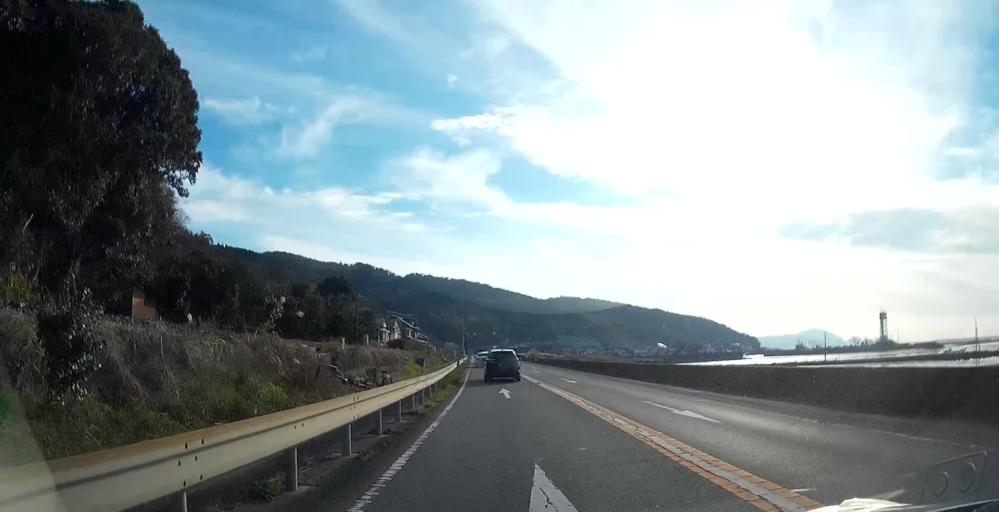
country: JP
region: Kumamoto
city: Uto
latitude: 32.6972
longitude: 130.5667
